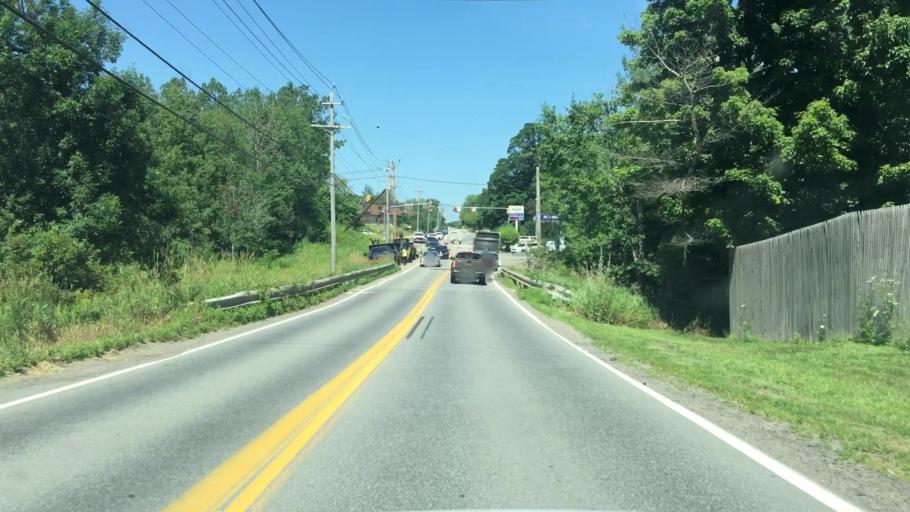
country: US
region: Maine
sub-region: Penobscot County
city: Bangor
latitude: 44.8234
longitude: -68.8077
